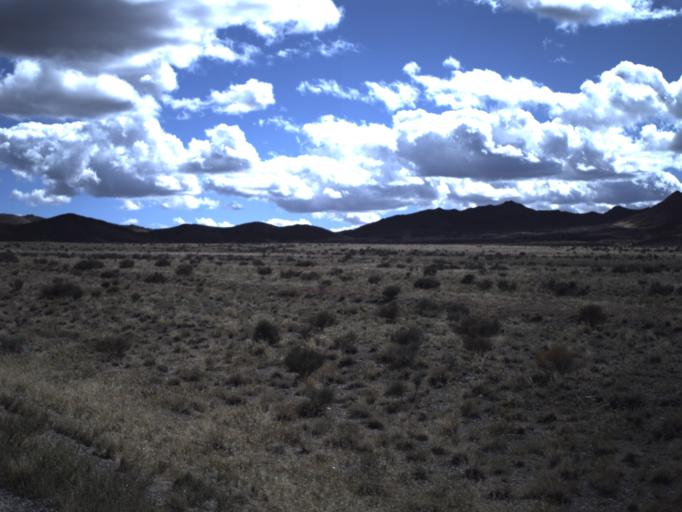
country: US
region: Utah
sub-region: Beaver County
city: Milford
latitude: 38.4417
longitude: -113.3202
